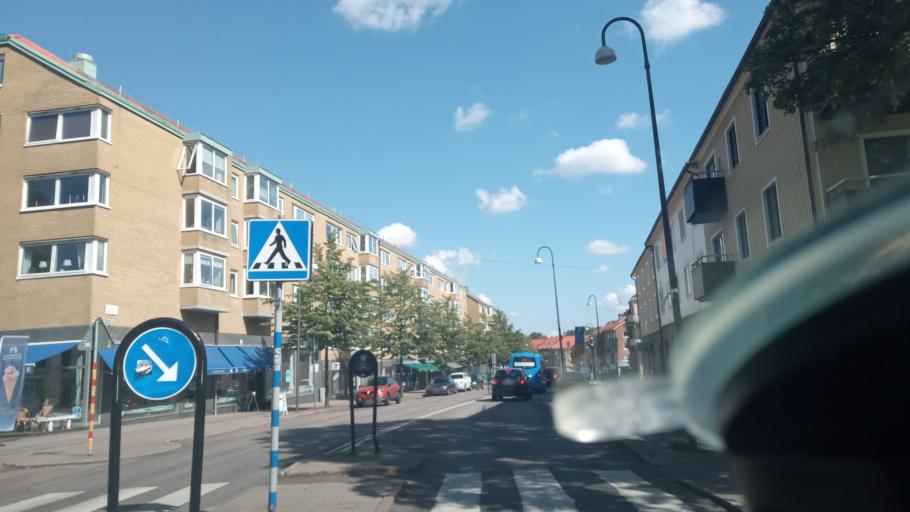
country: SE
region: Vaestra Goetaland
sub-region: Goteborg
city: Goeteborg
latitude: 57.7107
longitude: 12.0072
